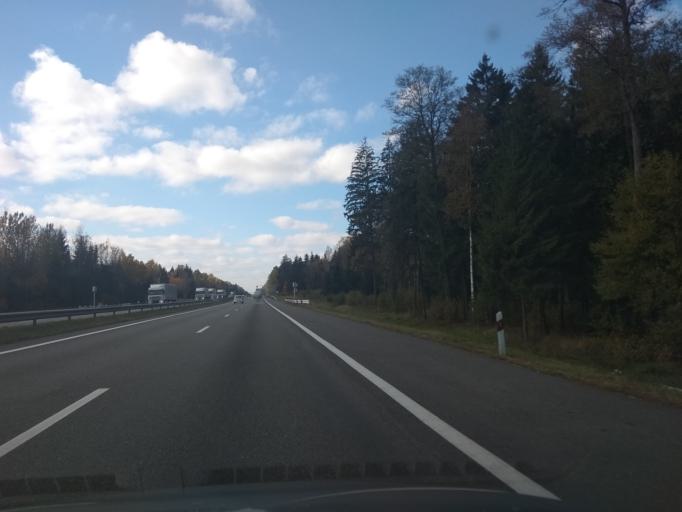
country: BY
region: Minsk
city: Enyerhyetykaw
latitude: 53.5396
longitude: 26.9068
